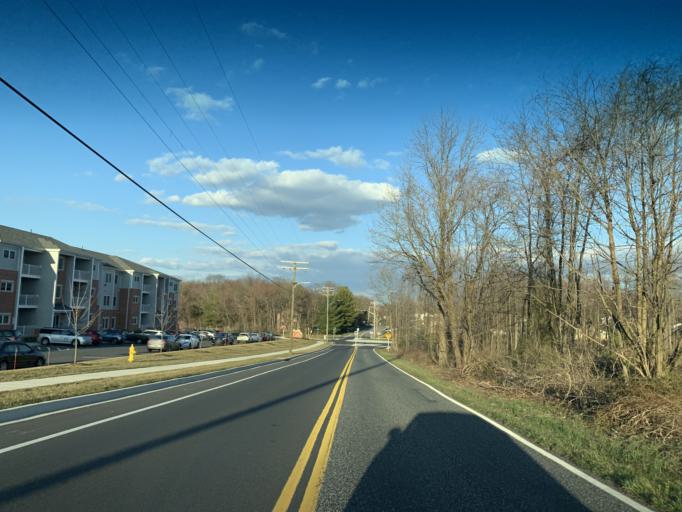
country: US
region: Maryland
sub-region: Harford County
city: Aberdeen
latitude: 39.5269
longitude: -76.1793
